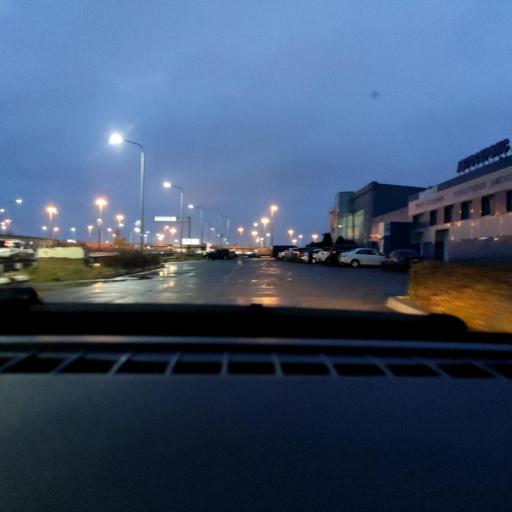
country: RU
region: Voronezj
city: Somovo
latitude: 51.6816
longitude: 39.3013
